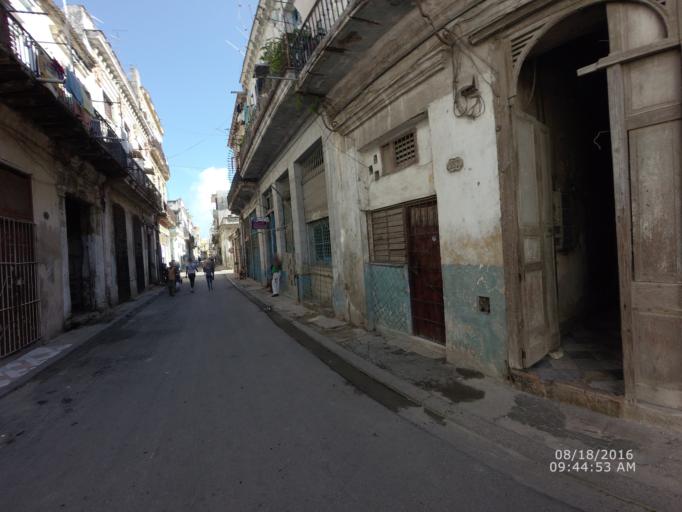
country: CU
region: La Habana
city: La Habana Vieja
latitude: 23.1334
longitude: -82.3496
